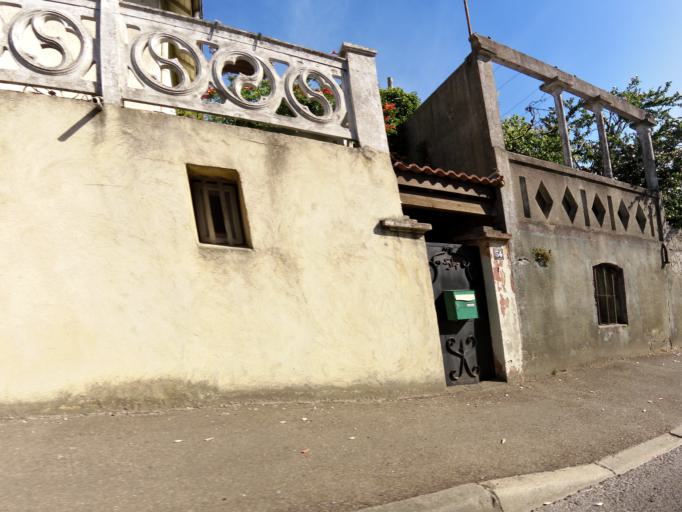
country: FR
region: Languedoc-Roussillon
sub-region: Departement du Gard
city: Nimes
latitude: 43.8441
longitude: 4.3446
